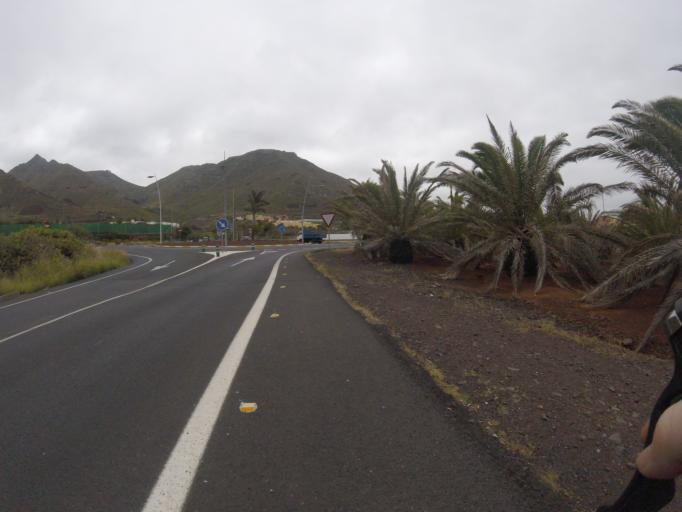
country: ES
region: Canary Islands
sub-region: Provincia de Santa Cruz de Tenerife
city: Tegueste
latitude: 28.5489
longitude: -16.3501
